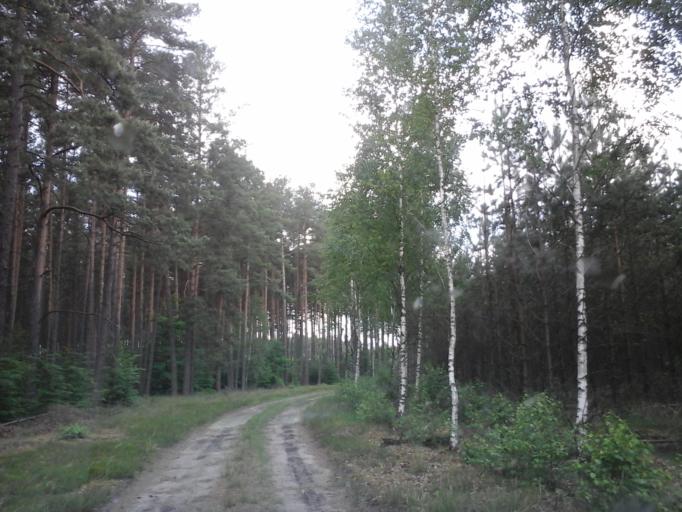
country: PL
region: West Pomeranian Voivodeship
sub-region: Powiat drawski
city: Kalisz Pomorski
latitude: 53.1687
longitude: 15.9030
